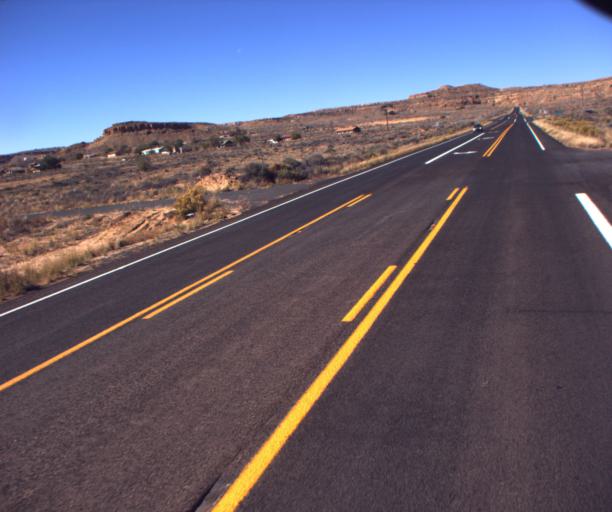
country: US
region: Arizona
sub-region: Navajo County
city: First Mesa
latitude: 35.8778
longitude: -110.6101
